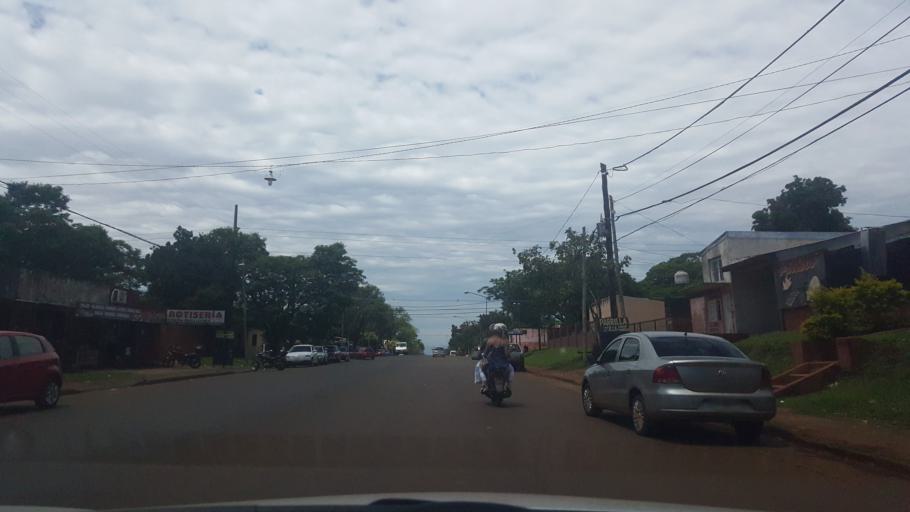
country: AR
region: Misiones
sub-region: Departamento de Capital
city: Posadas
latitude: -27.3793
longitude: -55.9153
